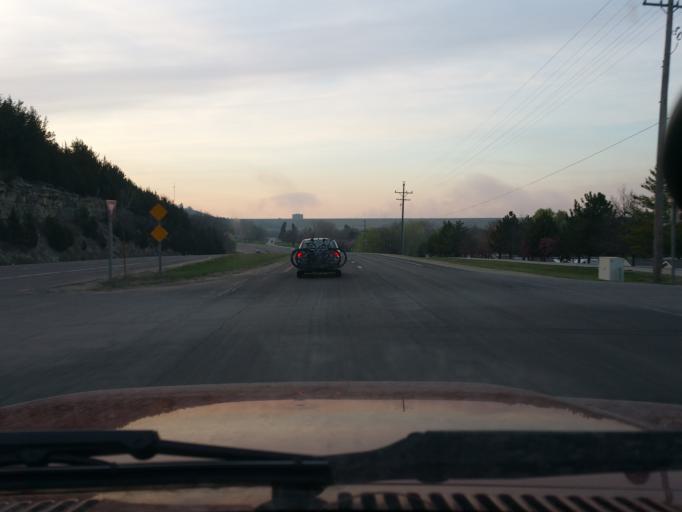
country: US
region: Kansas
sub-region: Riley County
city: Manhattan
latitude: 39.2419
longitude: -96.5930
